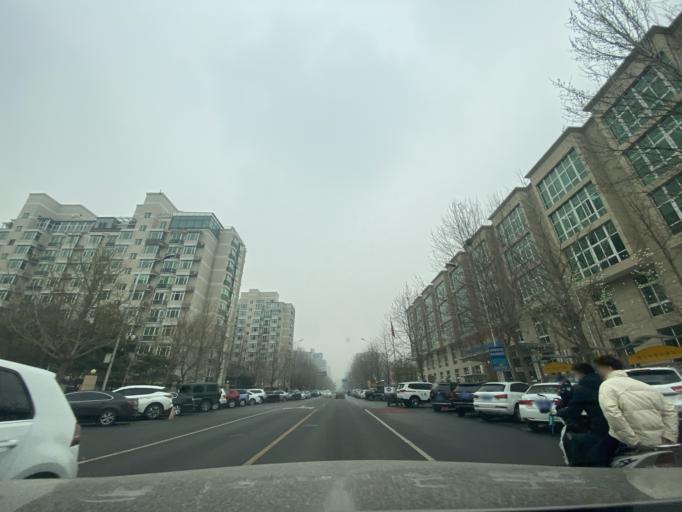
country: CN
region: Beijing
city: Sijiqing
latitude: 39.9648
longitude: 116.2737
